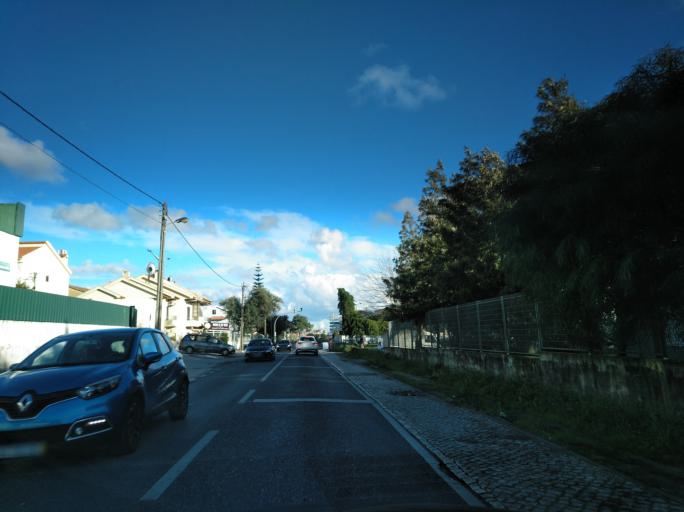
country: PT
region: Setubal
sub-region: Almada
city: Sobreda
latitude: 38.6489
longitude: -9.1845
